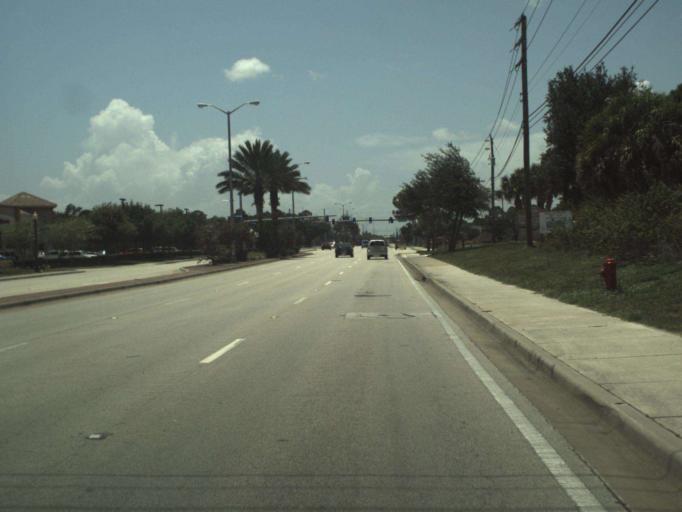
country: US
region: Florida
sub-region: Saint Lucie County
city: Port Saint Lucie
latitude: 27.2647
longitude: -80.4079
